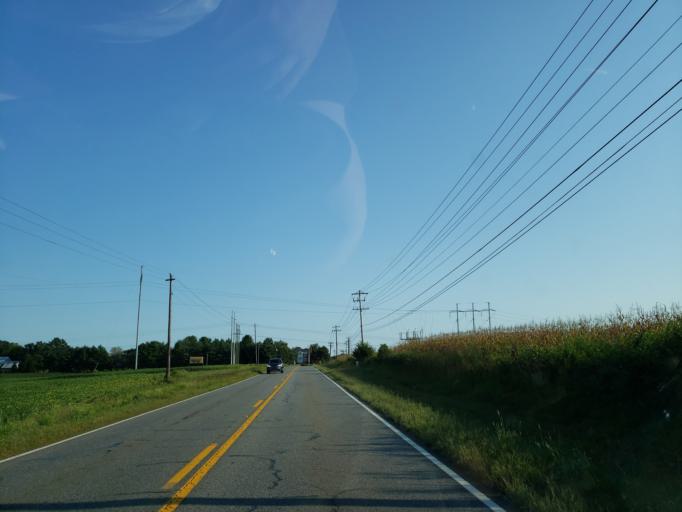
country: US
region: Georgia
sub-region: Murray County
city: Chatsworth
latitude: 34.7672
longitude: -84.8229
